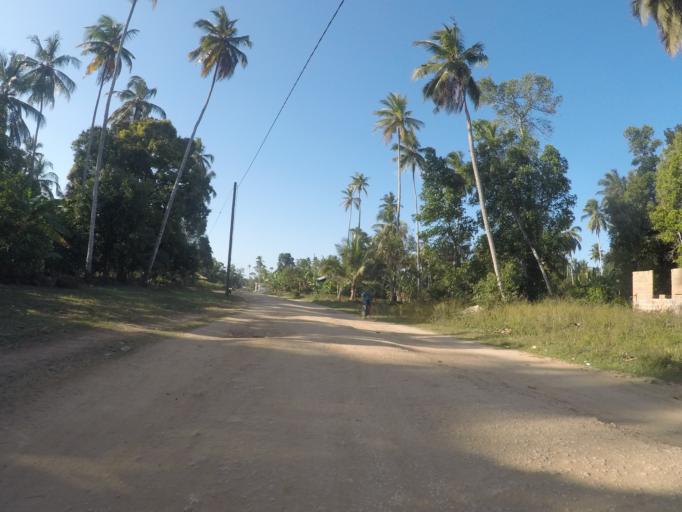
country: TZ
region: Zanzibar Central/South
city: Koani
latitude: -6.1585
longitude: 39.2873
